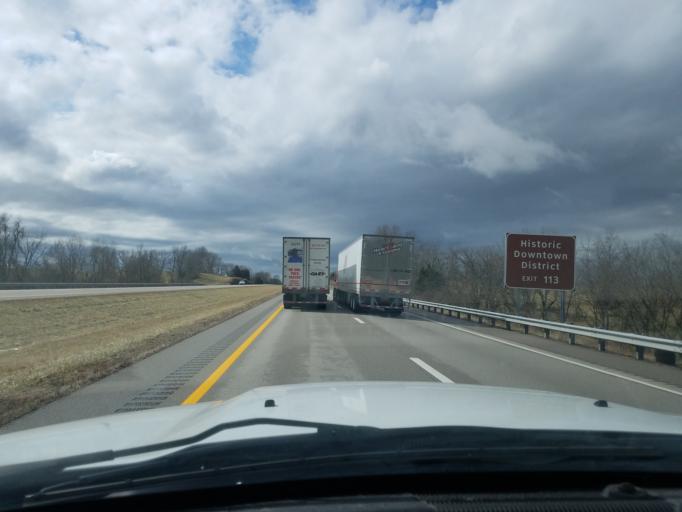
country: US
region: Kentucky
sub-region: Montgomery County
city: Mount Sterling
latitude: 38.0949
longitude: -83.8675
